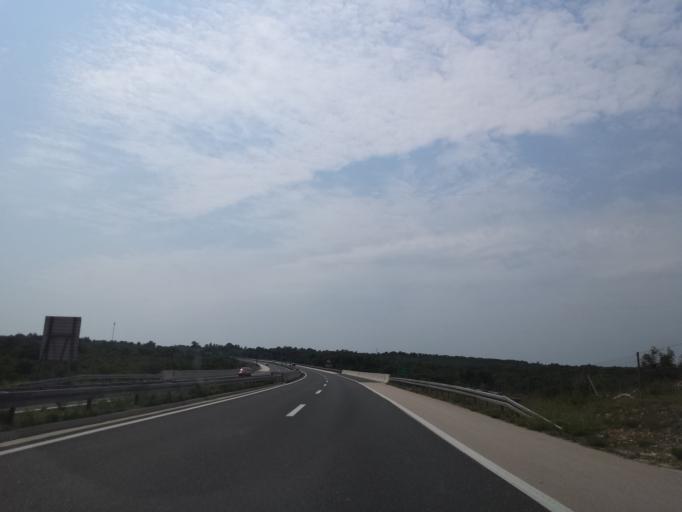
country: HR
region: Zadarska
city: Posedarje
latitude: 44.2148
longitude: 15.4504
